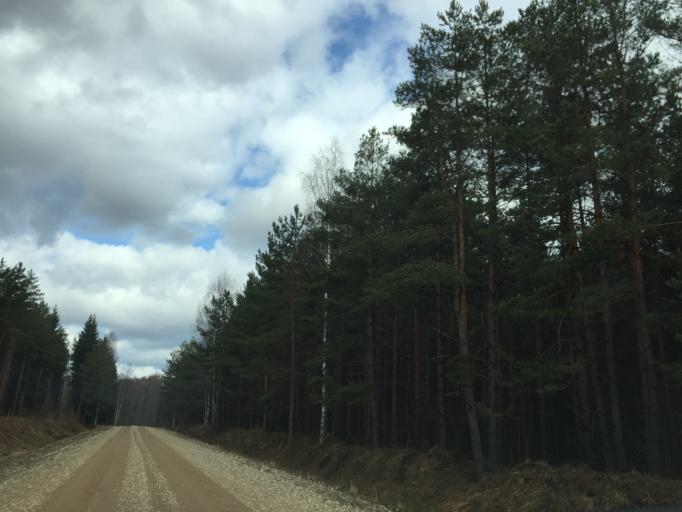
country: LV
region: Vecumnieki
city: Vecumnieki
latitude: 56.5975
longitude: 24.6397
